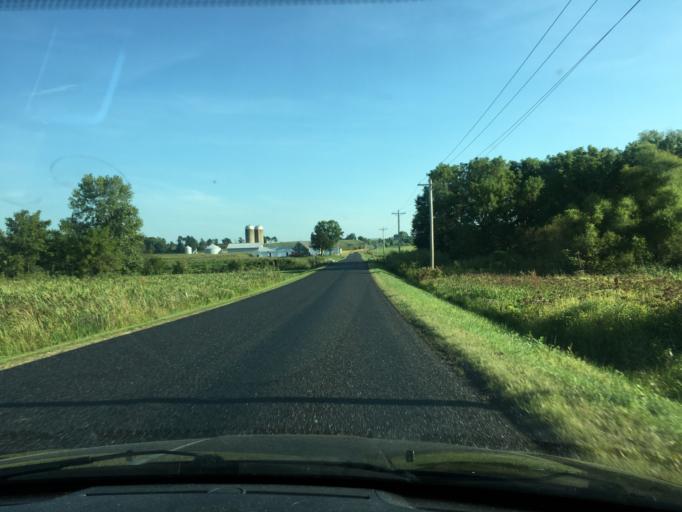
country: US
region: Ohio
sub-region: Logan County
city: West Liberty
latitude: 40.2821
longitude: -83.7262
